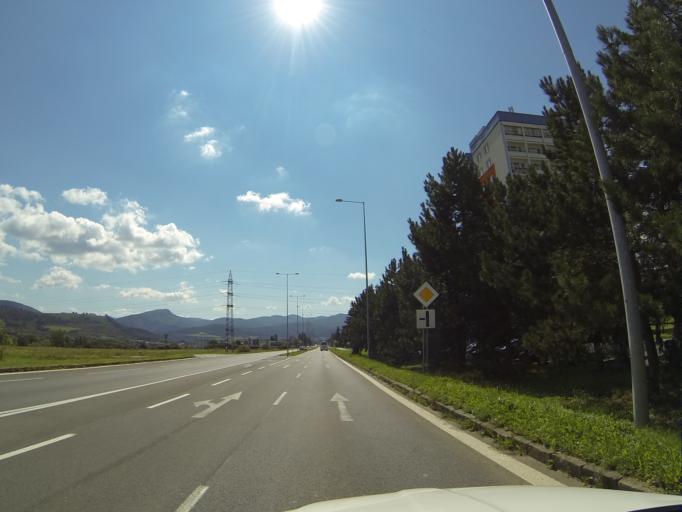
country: SK
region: Banskobystricky
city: Ziar nad Hronom
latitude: 48.6007
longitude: 18.8425
